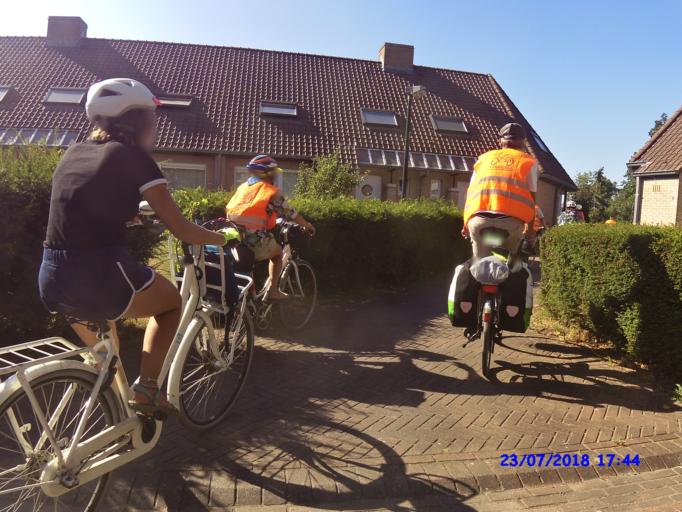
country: BE
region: Flanders
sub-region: Provincie West-Vlaanderen
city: Nieuwpoort
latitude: 51.0743
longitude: 2.7946
